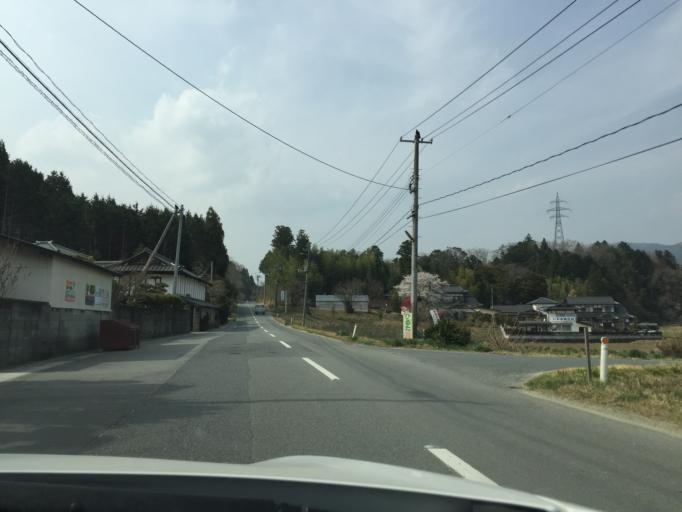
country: JP
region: Fukushima
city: Iwaki
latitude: 37.0222
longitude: 140.7304
